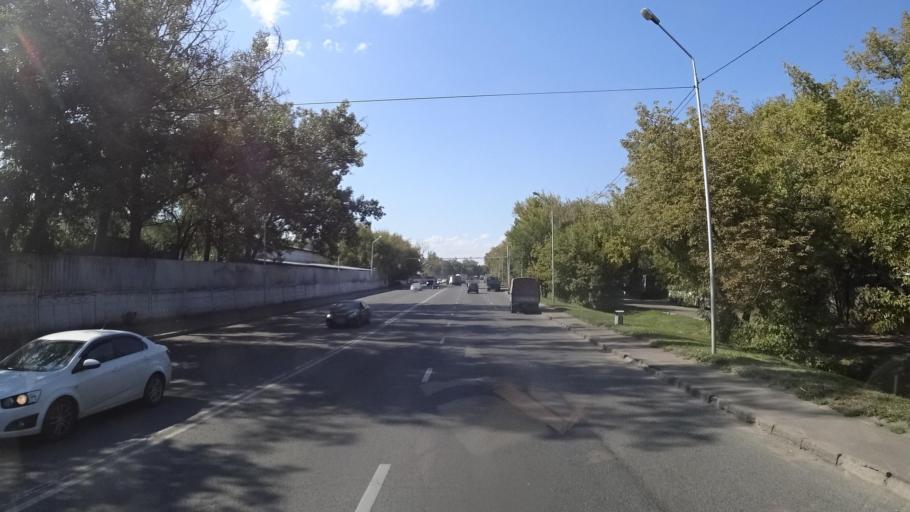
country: KZ
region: Almaty Oblysy
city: Pervomayskiy
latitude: 43.3434
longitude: 76.9756
